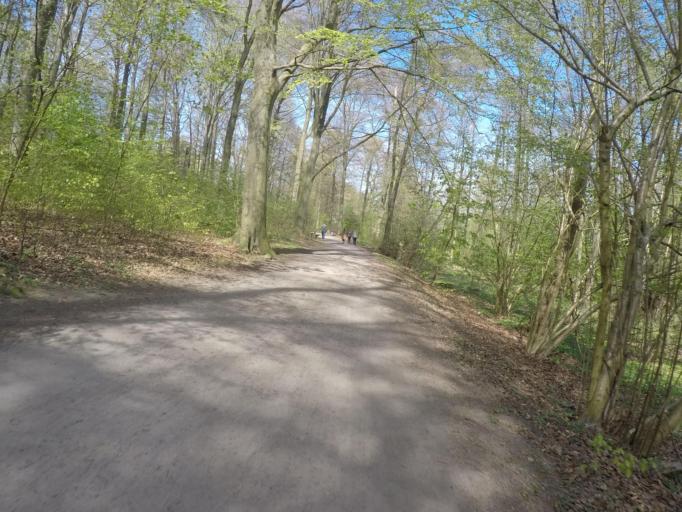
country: DE
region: Hamburg
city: Poppenbuettel
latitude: 53.6507
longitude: 10.0803
